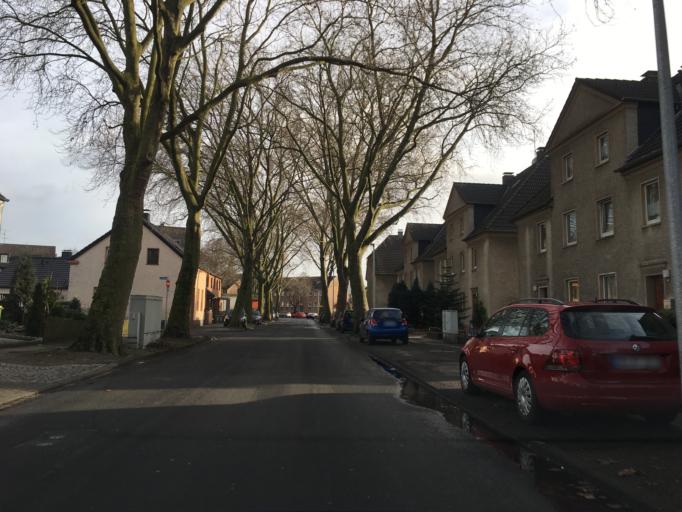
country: DE
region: North Rhine-Westphalia
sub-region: Regierungsbezirk Dusseldorf
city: Oberhausen
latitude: 51.4777
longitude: 6.8241
